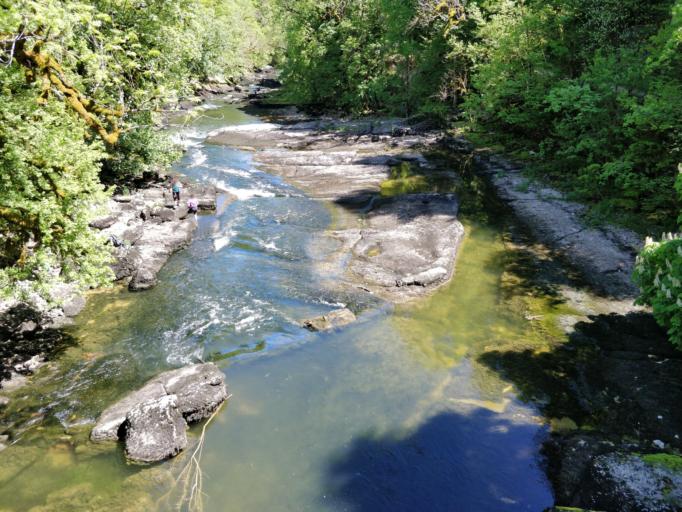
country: CH
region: Neuchatel
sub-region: Le Locle District
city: Les Brenets
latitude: 47.0849
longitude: 6.7105
